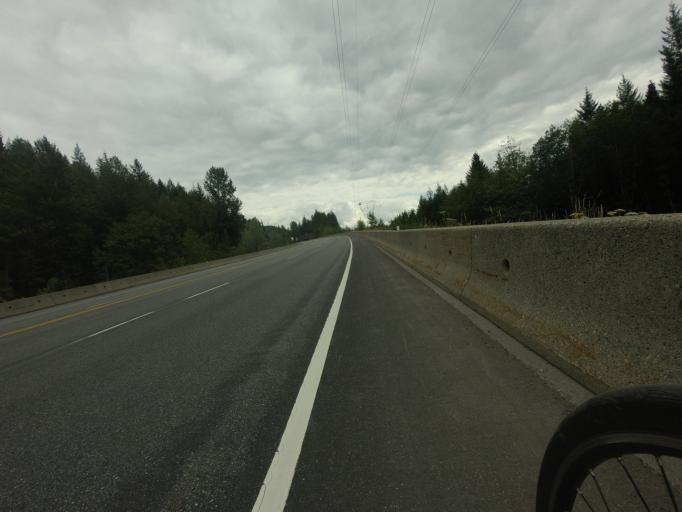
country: CA
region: British Columbia
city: Whistler
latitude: 49.8582
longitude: -123.1560
